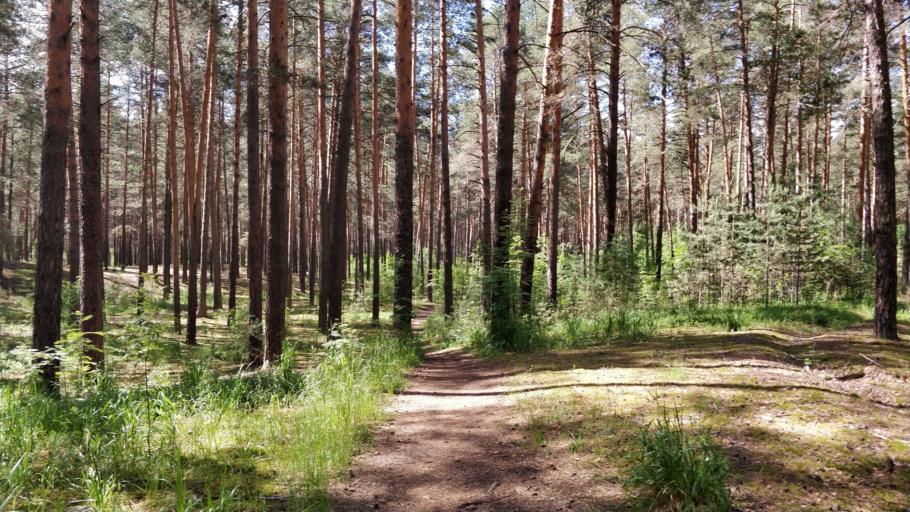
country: RU
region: Perm
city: Perm
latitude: 58.0622
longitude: 56.3010
